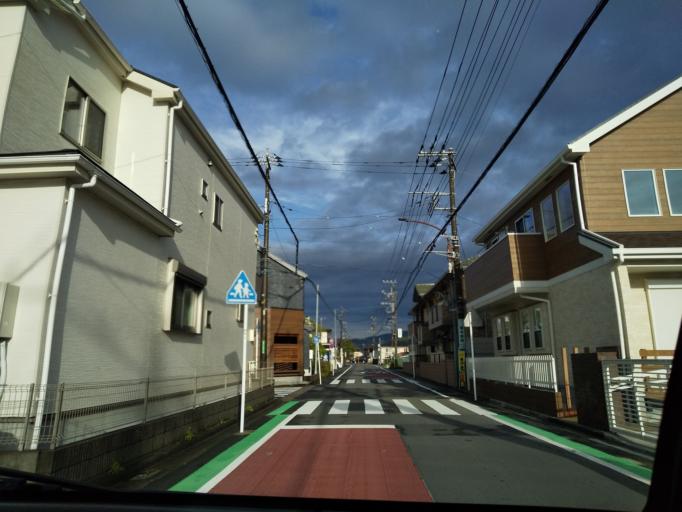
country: JP
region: Tokyo
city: Hachioji
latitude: 35.6024
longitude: 139.3273
